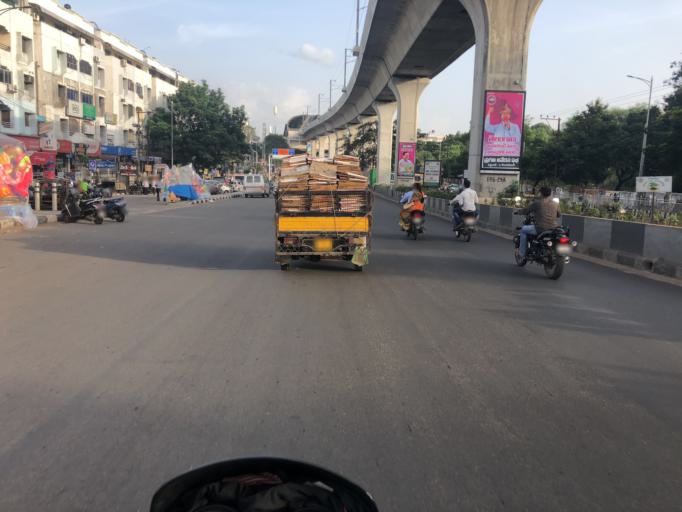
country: IN
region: Telangana
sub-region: Rangareddi
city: Kukatpalli
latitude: 17.4500
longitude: 78.4371
